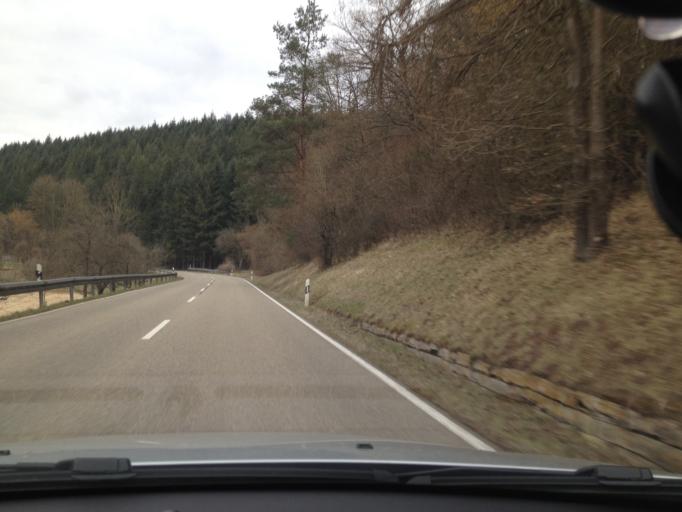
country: DE
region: Baden-Wuerttemberg
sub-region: Regierungsbezirk Stuttgart
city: Kulsheim
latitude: 49.7162
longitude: 9.5465
